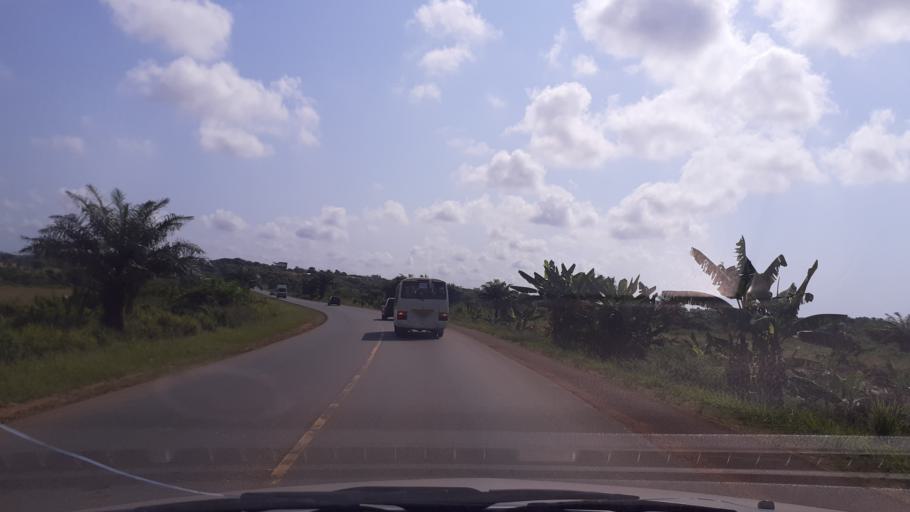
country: LR
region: Montserrado
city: Bensonville City
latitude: 6.2094
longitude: -10.5637
